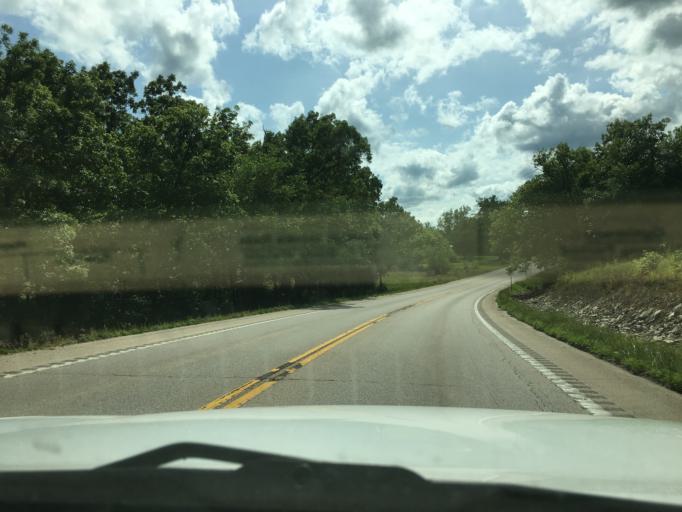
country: US
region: Missouri
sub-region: Franklin County
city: Gerald
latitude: 38.3948
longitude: -91.3419
